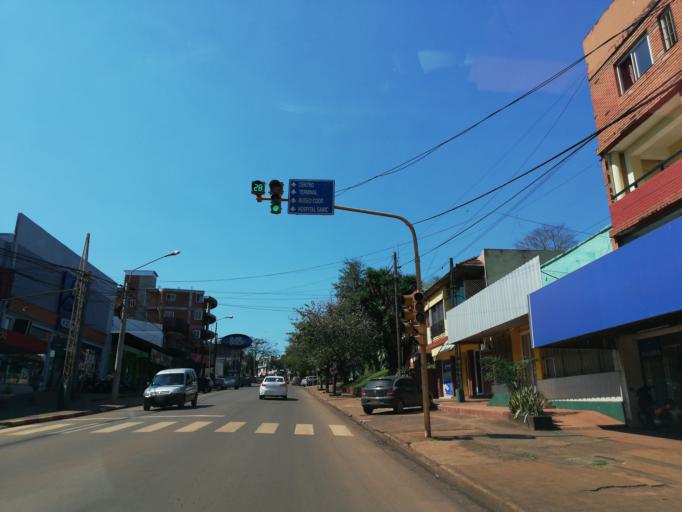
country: AR
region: Misiones
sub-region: Departamento de Eldorado
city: Eldorado
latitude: -26.4069
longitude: -54.6123
